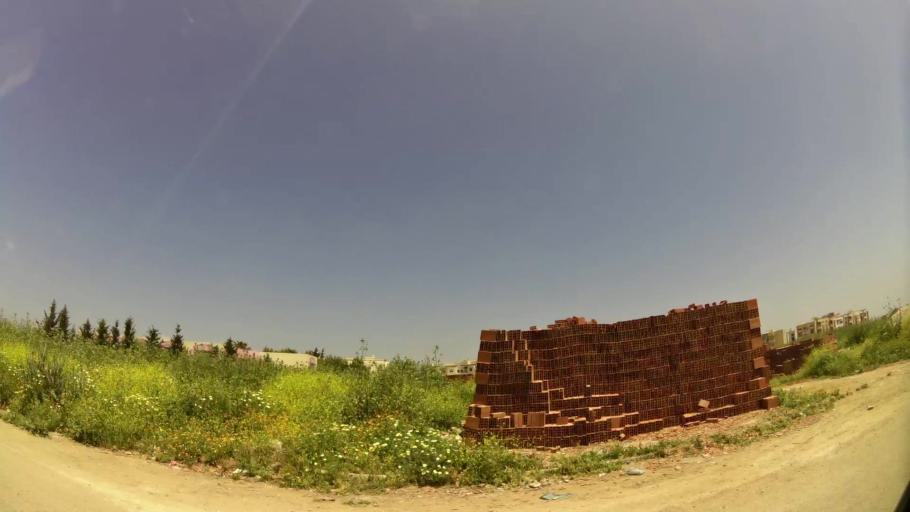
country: MA
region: Fes-Boulemane
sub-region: Fes
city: Fes
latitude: 34.0326
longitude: -5.0425
